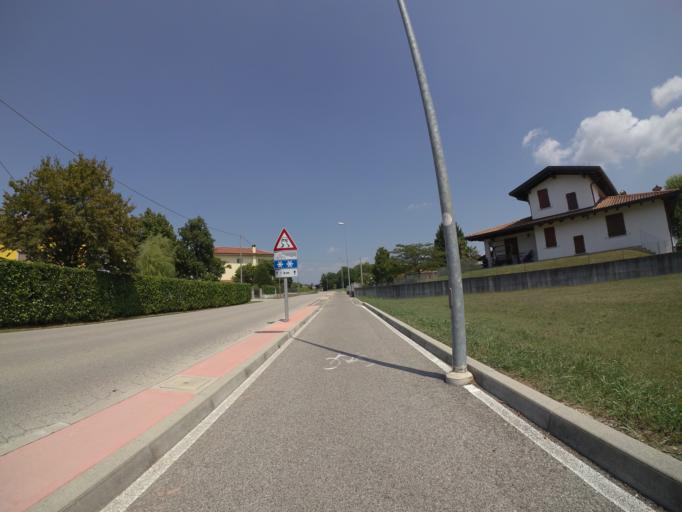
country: IT
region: Friuli Venezia Giulia
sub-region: Provincia di Udine
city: Sedegliano
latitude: 46.0038
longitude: 12.9677
